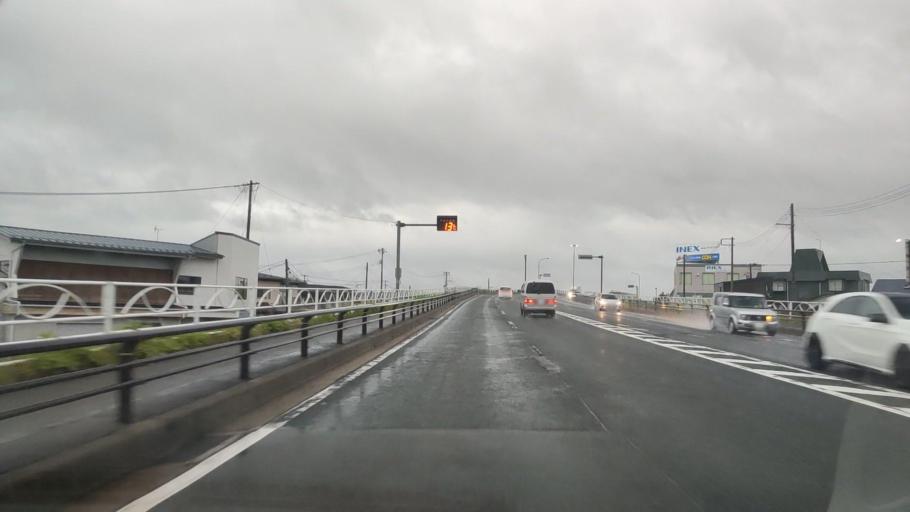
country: JP
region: Akita
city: Akita
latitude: 39.6983
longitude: 140.1164
